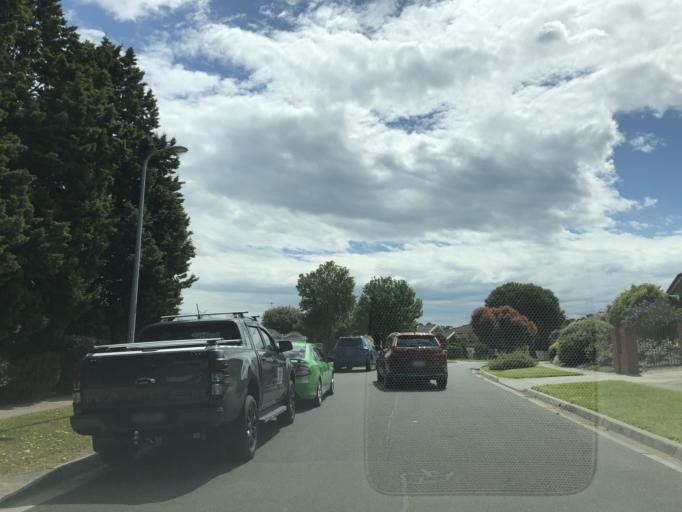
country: AU
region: Victoria
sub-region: Casey
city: Endeavour Hills
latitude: -37.9667
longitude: 145.2729
